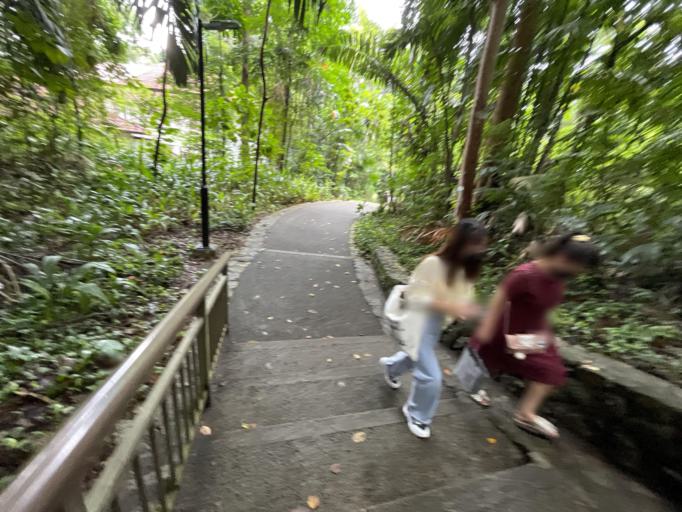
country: SG
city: Singapore
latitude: 1.2681
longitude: 103.8214
